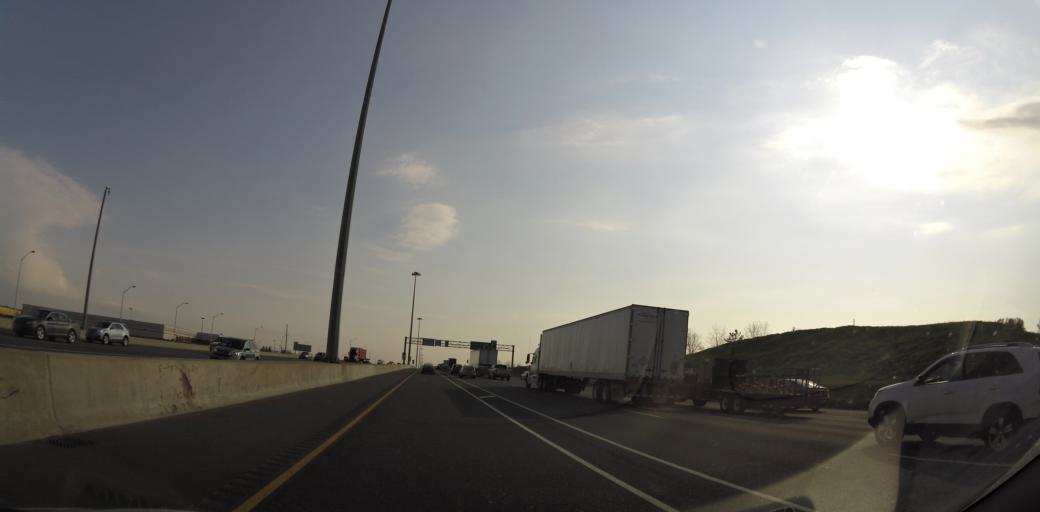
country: CA
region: Ontario
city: Oakville
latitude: 43.4025
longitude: -79.7489
